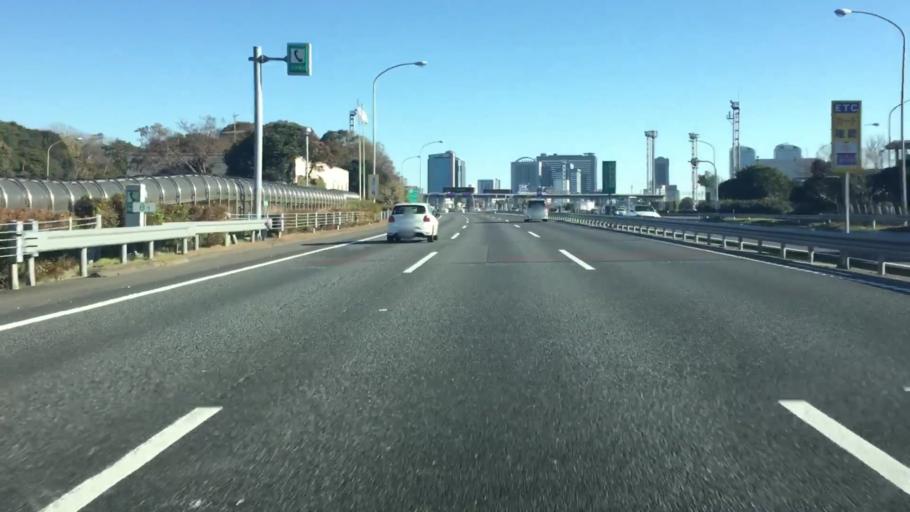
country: JP
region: Chiba
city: Funabashi
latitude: 35.6611
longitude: 140.0195
